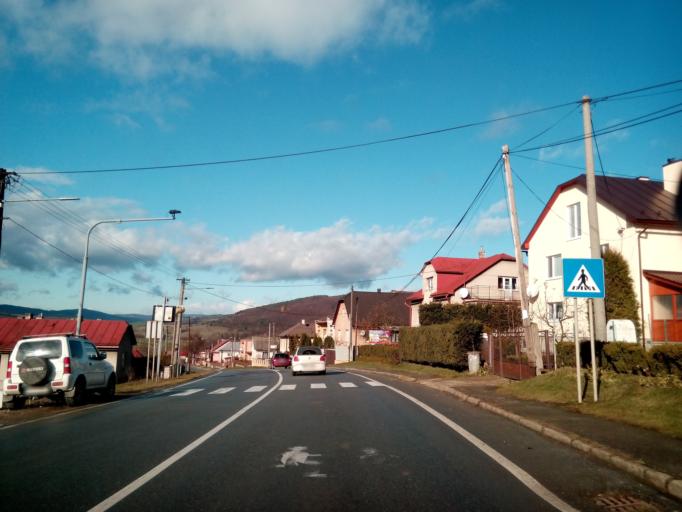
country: SK
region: Presovsky
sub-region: Okres Bardejov
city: Bardejov
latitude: 49.2465
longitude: 21.2613
